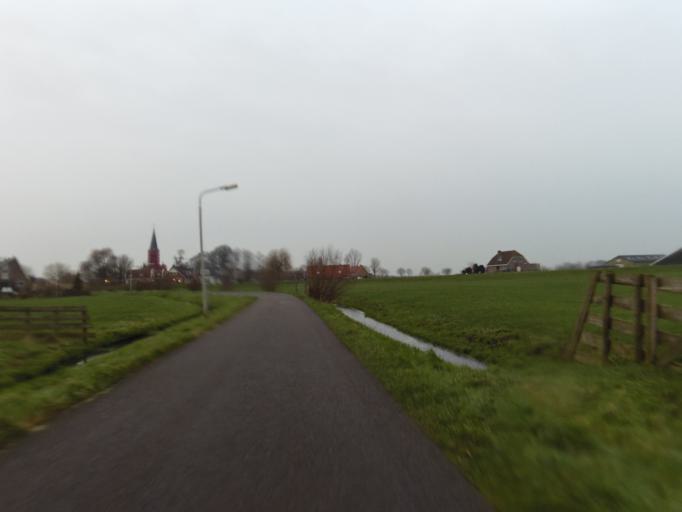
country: NL
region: South Holland
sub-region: Gemeente Leiderdorp
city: Leiderdorp
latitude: 52.1890
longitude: 4.5671
